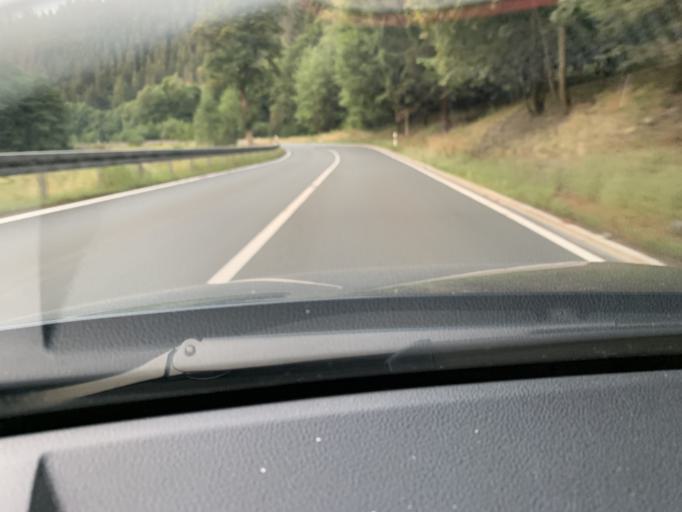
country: DE
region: Thuringia
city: Judenbach
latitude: 50.4043
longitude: 11.1890
